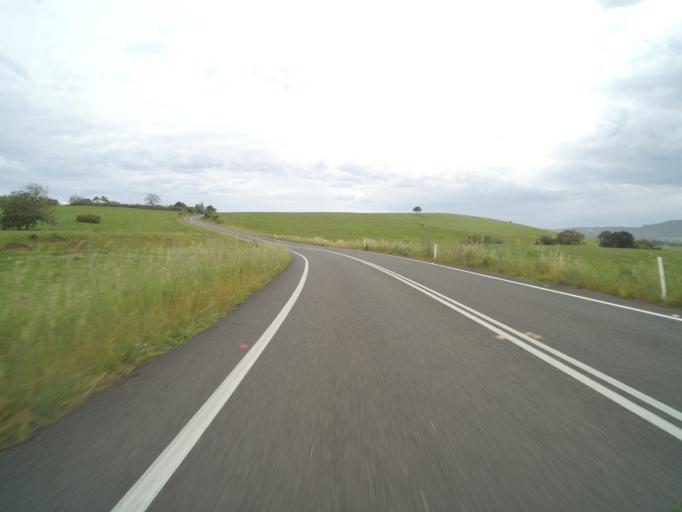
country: AU
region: New South Wales
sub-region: Kiama
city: Kiama
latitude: -34.6584
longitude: 150.8184
